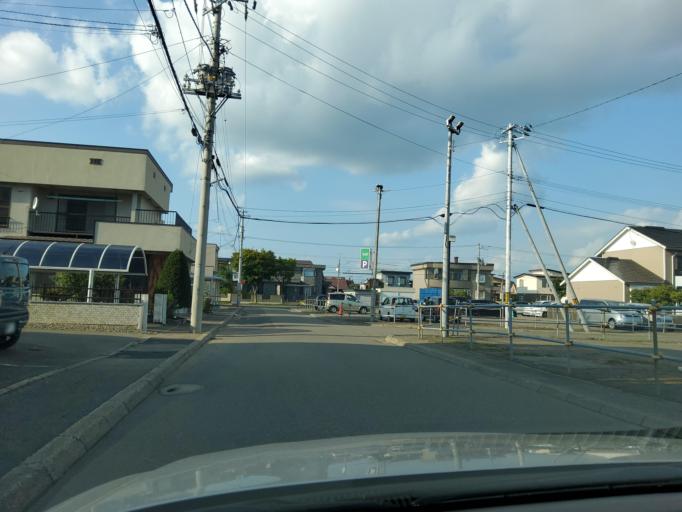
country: JP
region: Hokkaido
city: Obihiro
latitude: 42.9115
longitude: 143.1708
